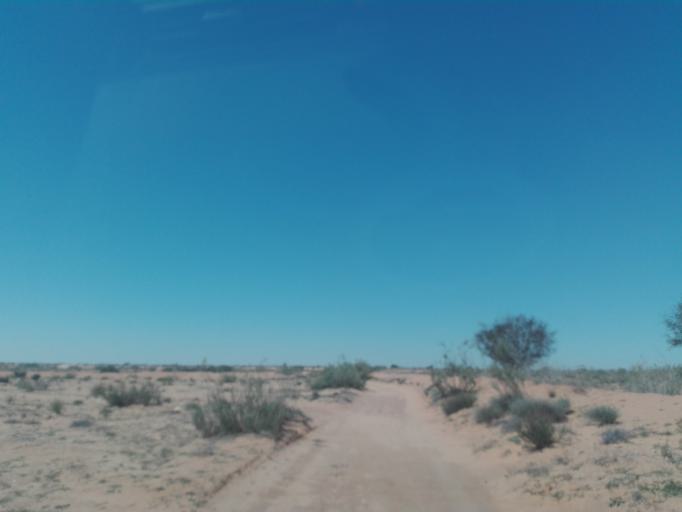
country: TN
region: Safaqis
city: Bi'r `Ali Bin Khalifah
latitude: 34.7899
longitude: 10.2740
